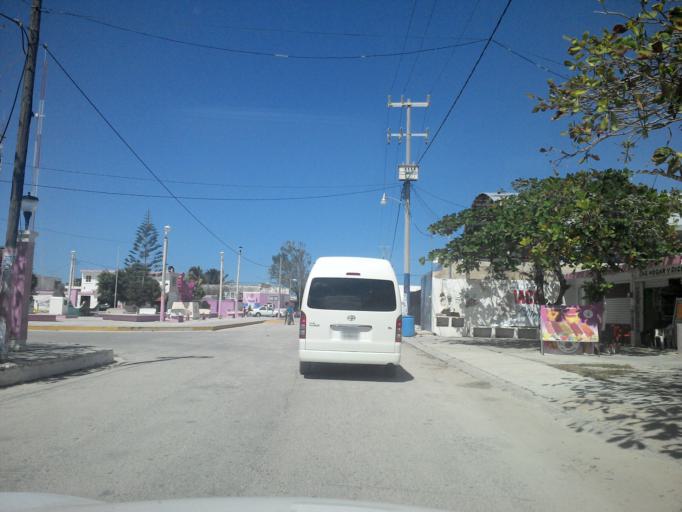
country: MX
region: Yucatan
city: Telchac Puerto
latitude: 21.3422
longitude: -89.2636
